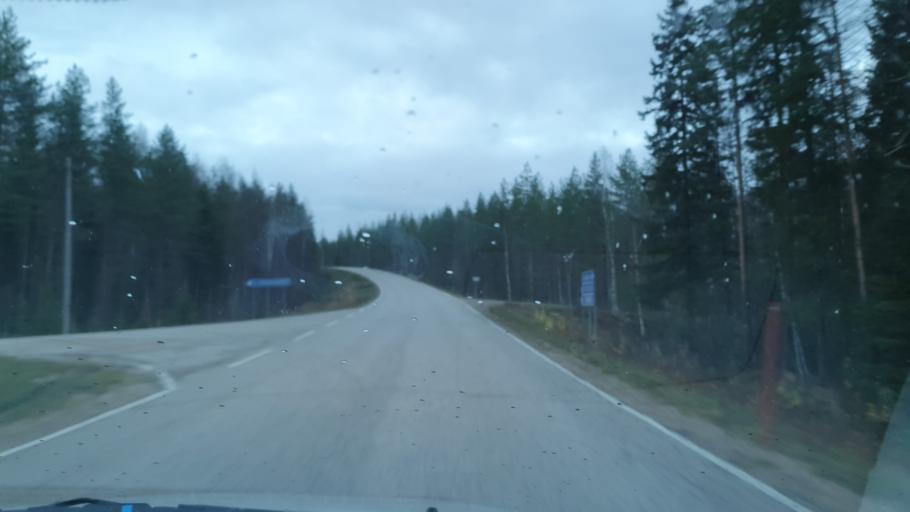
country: FI
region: Kainuu
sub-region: Kajaani
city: Ristijaervi
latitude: 64.4381
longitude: 28.3692
